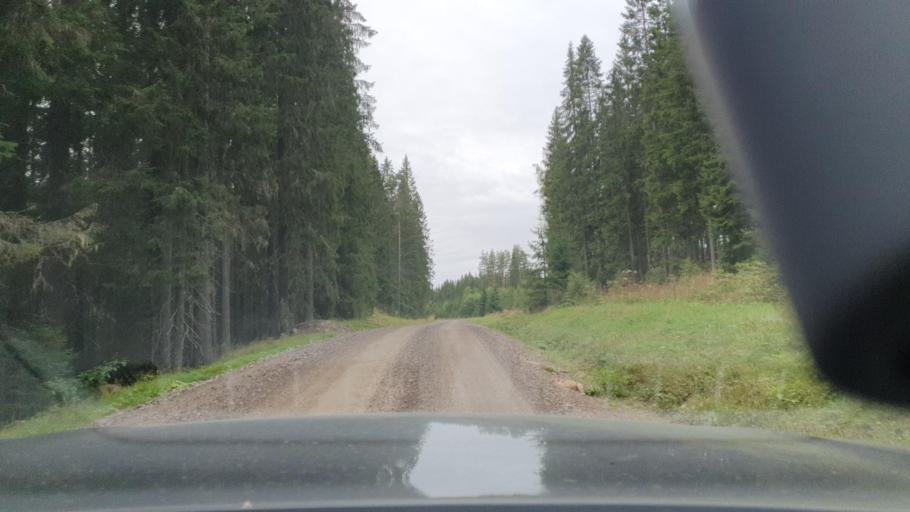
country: SE
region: Vaermland
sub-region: Eda Kommun
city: Charlottenberg
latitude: 60.0361
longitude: 12.5925
